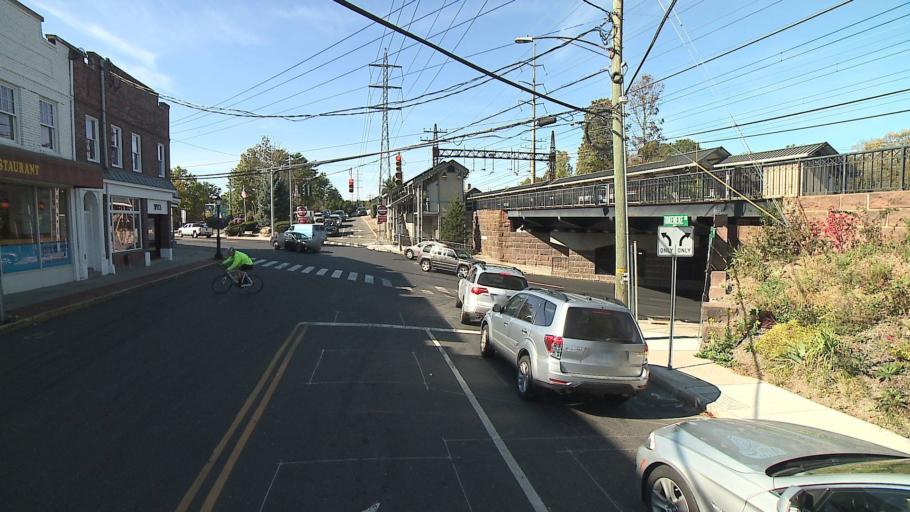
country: US
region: Connecticut
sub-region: Fairfield County
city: Darien
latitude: 41.0770
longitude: -73.4701
